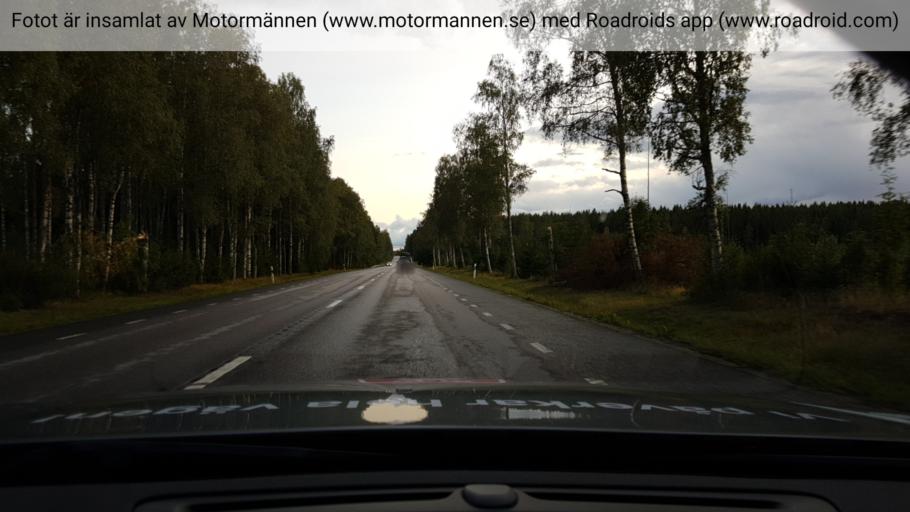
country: SE
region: OErebro
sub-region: Hallefors Kommun
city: Haellefors
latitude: 59.7630
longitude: 14.5183
